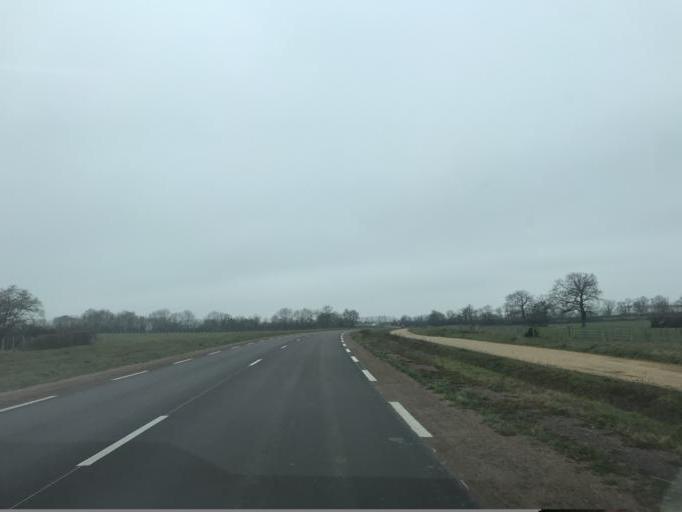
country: FR
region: Bourgogne
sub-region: Departement de l'Yonne
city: Avallon
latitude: 47.5018
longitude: 3.9185
